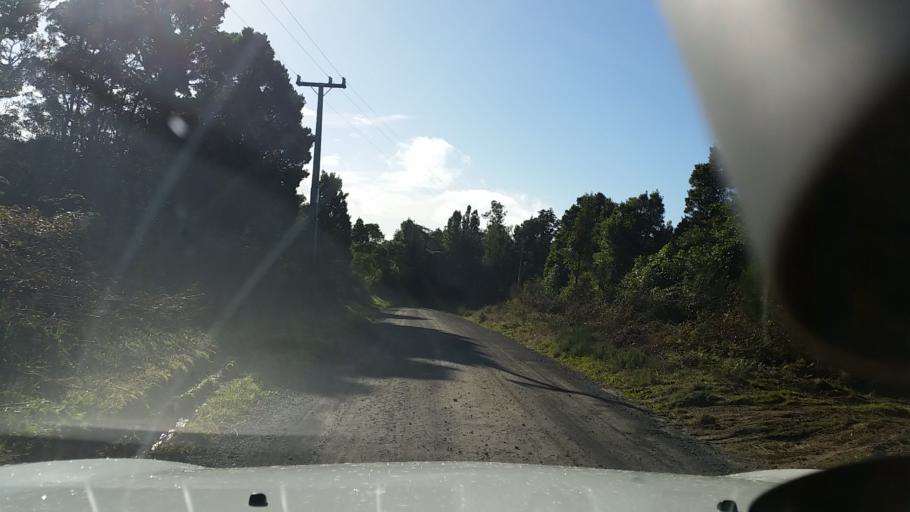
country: NZ
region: Bay of Plenty
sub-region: Kawerau District
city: Kawerau
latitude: -38.0187
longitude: 176.4717
